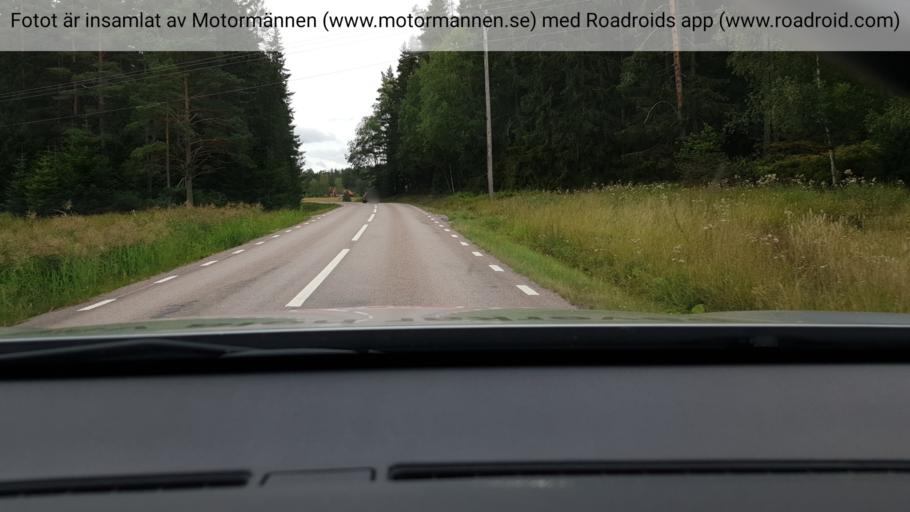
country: SE
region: Soedermanland
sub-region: Nykopings Kommun
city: Nykoping
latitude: 58.8546
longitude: 17.0596
